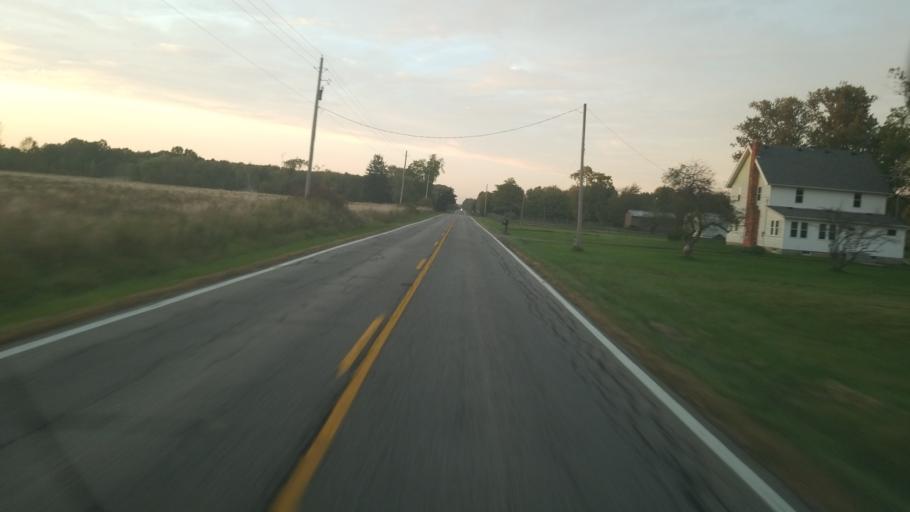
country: US
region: Ohio
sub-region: Ashtabula County
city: Andover
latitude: 41.6418
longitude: -80.6669
